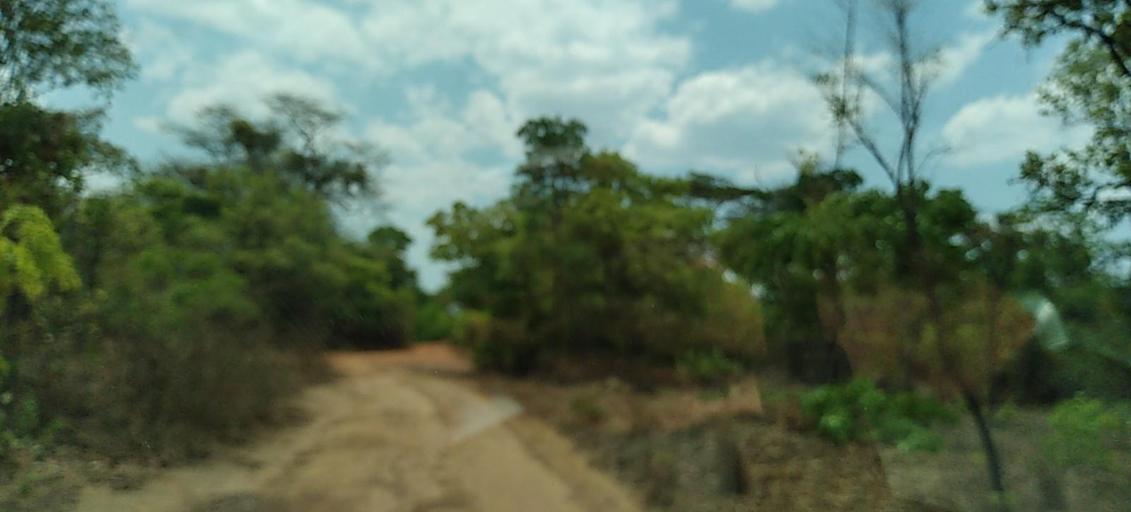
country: ZM
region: Copperbelt
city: Chililabombwe
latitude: -12.5281
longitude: 27.6280
